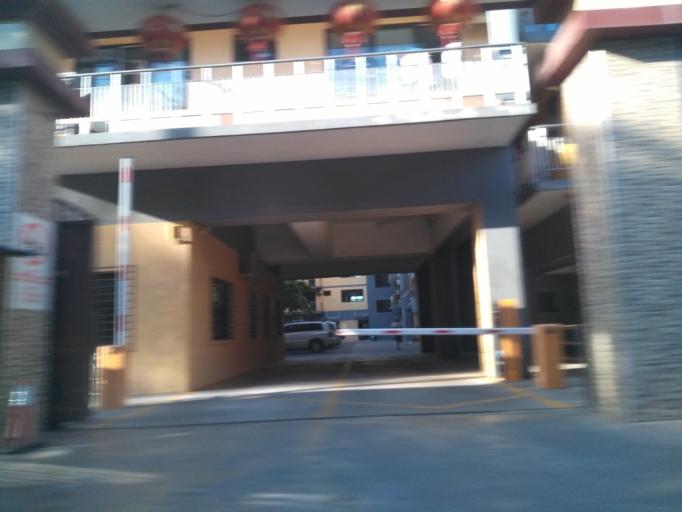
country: TZ
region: Dar es Salaam
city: Magomeni
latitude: -6.7616
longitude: 39.2609
